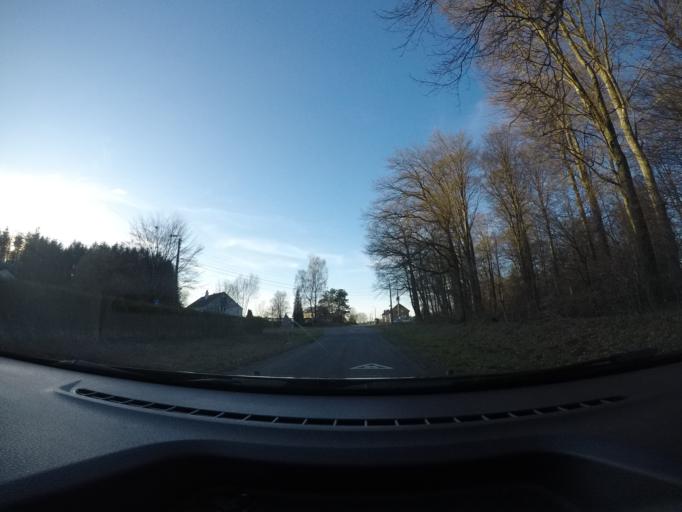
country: BE
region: Wallonia
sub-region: Province du Luxembourg
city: Tintigny
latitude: 49.6762
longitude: 5.4835
